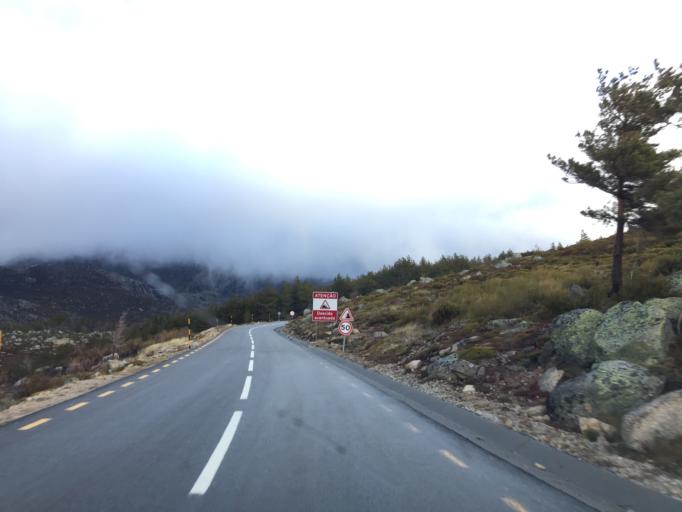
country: PT
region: Castelo Branco
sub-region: Covilha
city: Covilha
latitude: 40.3179
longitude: -7.5744
